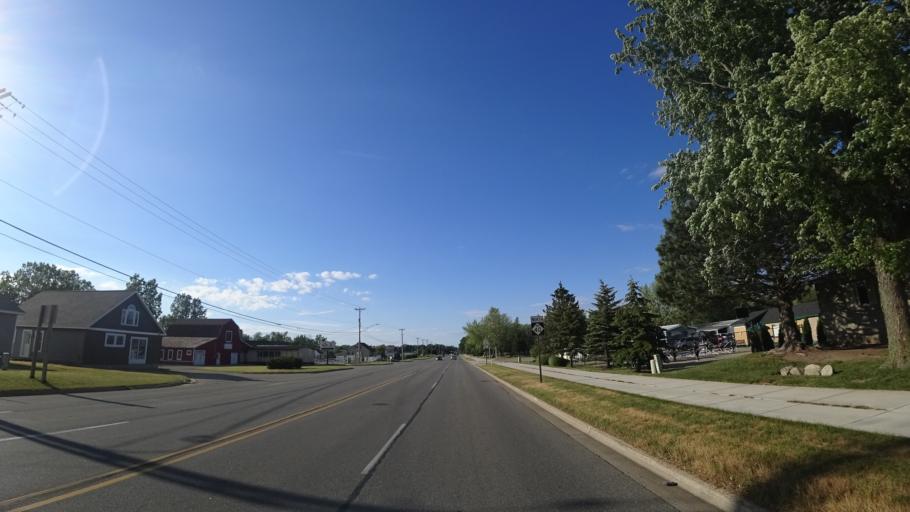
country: US
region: Michigan
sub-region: Ottawa County
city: Holland
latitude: 42.7552
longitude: -86.0967
